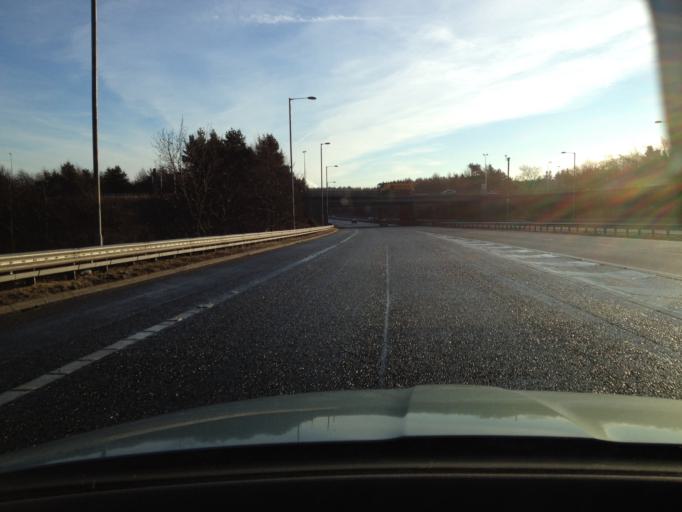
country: GB
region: Scotland
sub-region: West Lothian
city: Livingston
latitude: 55.9166
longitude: -3.5279
